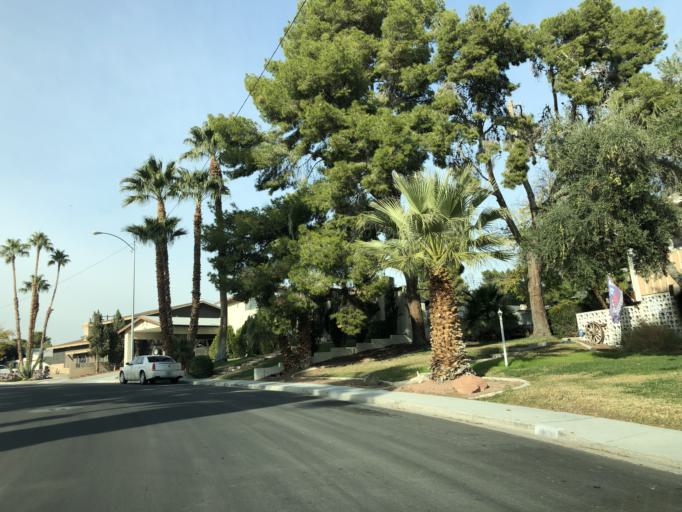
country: US
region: Nevada
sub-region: Clark County
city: Winchester
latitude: 36.1238
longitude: -115.1214
